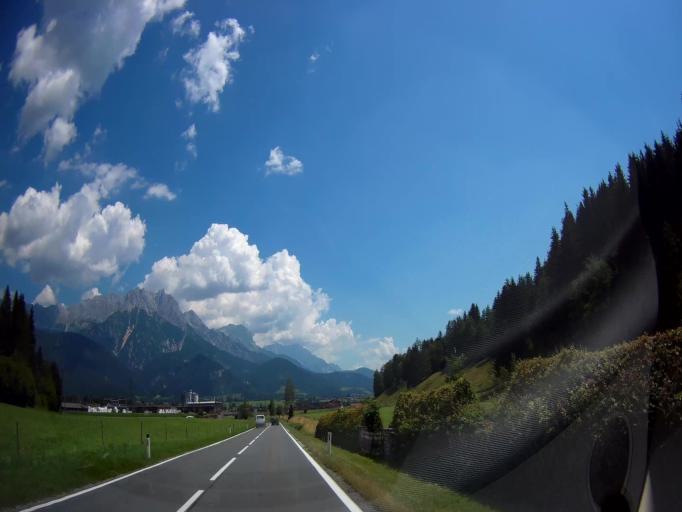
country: AT
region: Salzburg
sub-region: Politischer Bezirk Zell am See
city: Leogang
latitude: 47.4417
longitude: 12.8047
